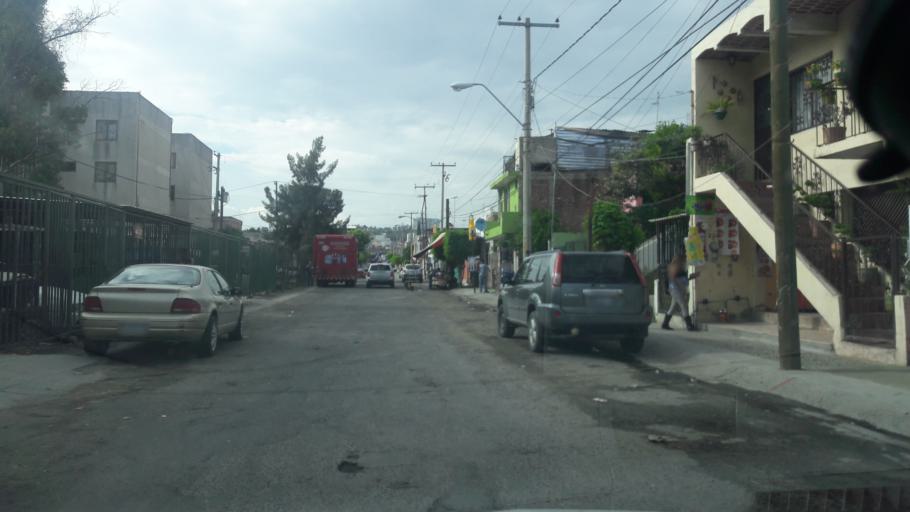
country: MX
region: Guanajuato
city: Leon
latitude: 21.1435
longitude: -101.6986
